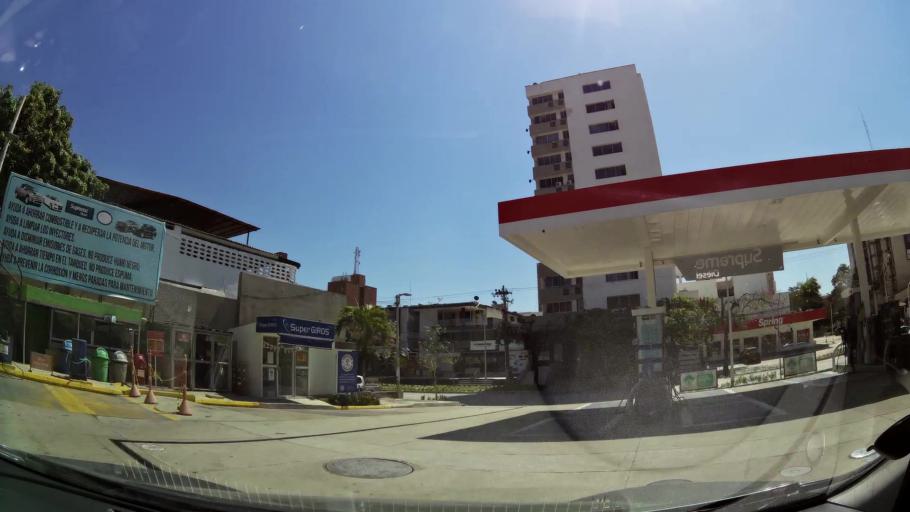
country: CO
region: Atlantico
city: Barranquilla
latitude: 11.0026
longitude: -74.8065
